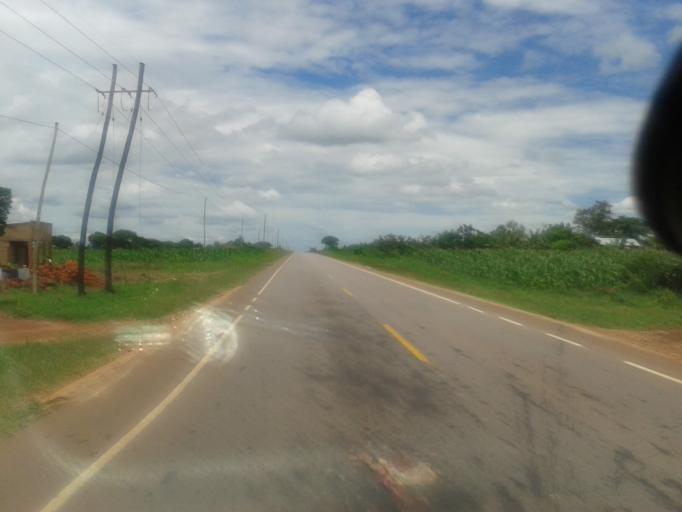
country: UG
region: Western Region
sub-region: Kiryandongo District
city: Masindi Port
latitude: 1.7766
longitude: 32.0182
